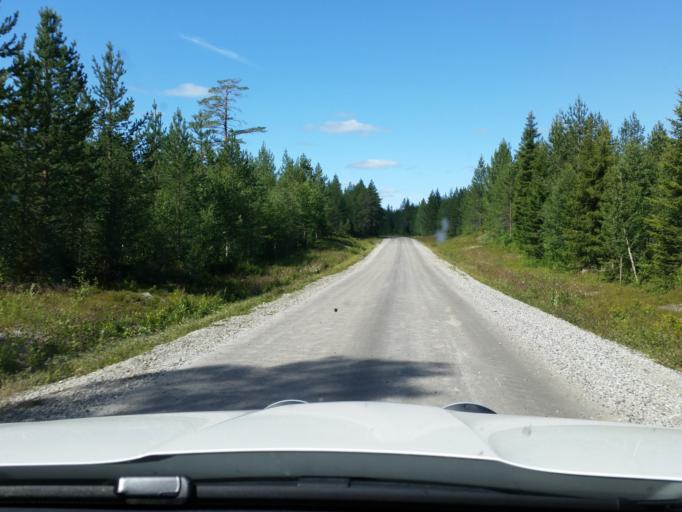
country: SE
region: Vaesterbotten
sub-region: Skelleftea Kommun
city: Storvik
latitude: 65.2186
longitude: 20.9264
